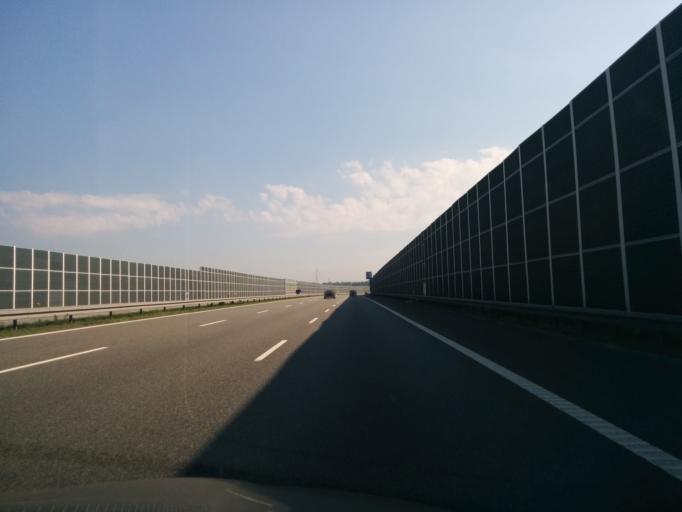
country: PL
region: Silesian Voivodeship
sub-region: Powiat tarnogorski
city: Wieszowa
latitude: 50.3623
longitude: 18.7295
